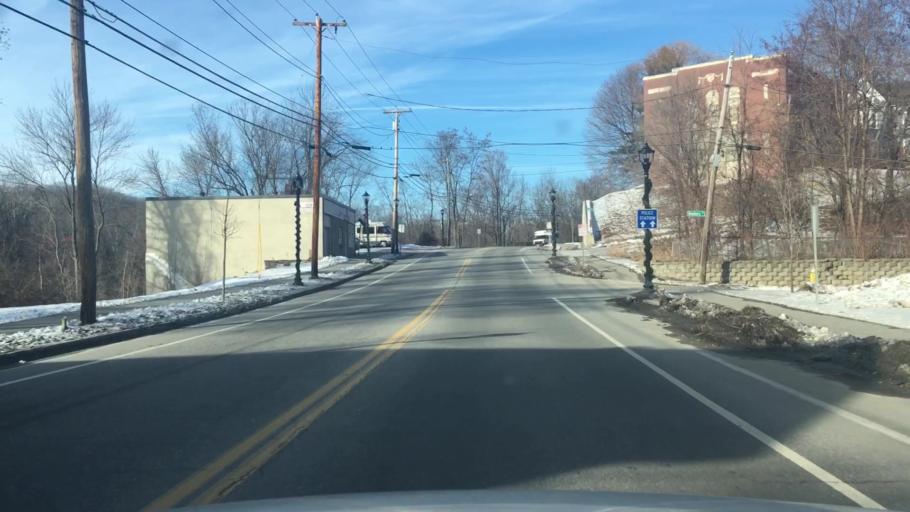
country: US
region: Maine
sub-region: Androscoggin County
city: Auburn
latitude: 44.0886
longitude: -70.2257
